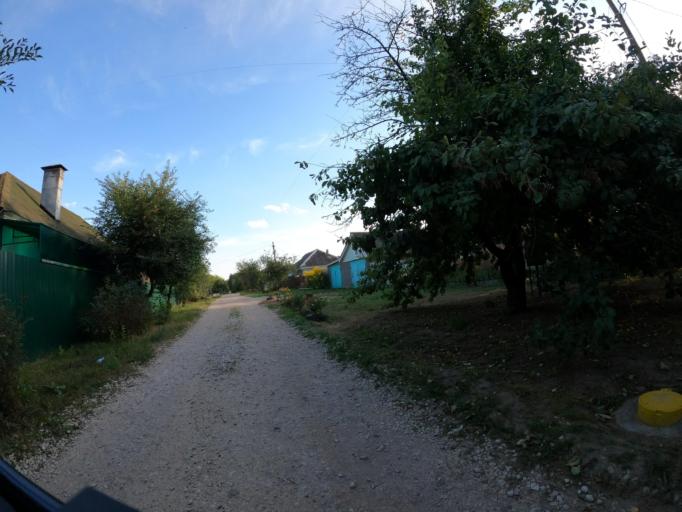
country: RU
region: Moskovskaya
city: Raduzhnyy
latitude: 55.1082
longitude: 38.7302
